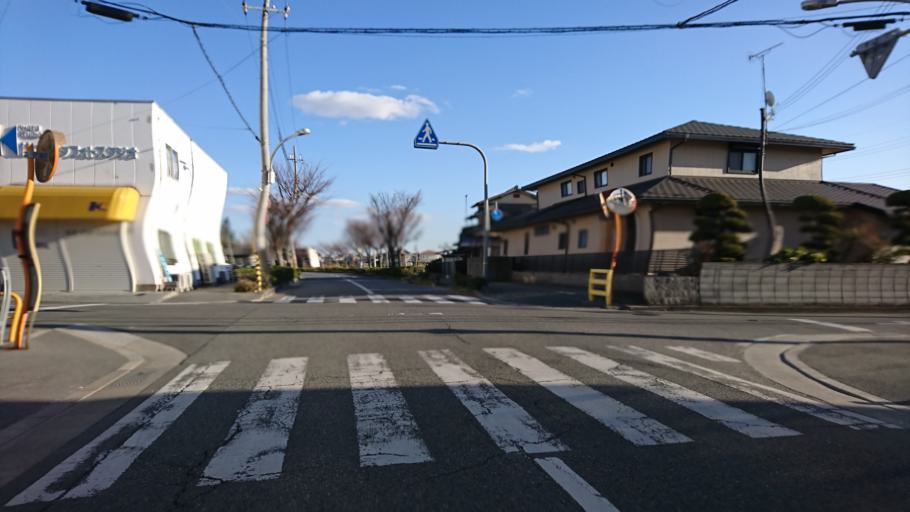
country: JP
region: Hyogo
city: Kakogawacho-honmachi
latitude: 34.7479
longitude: 134.8216
